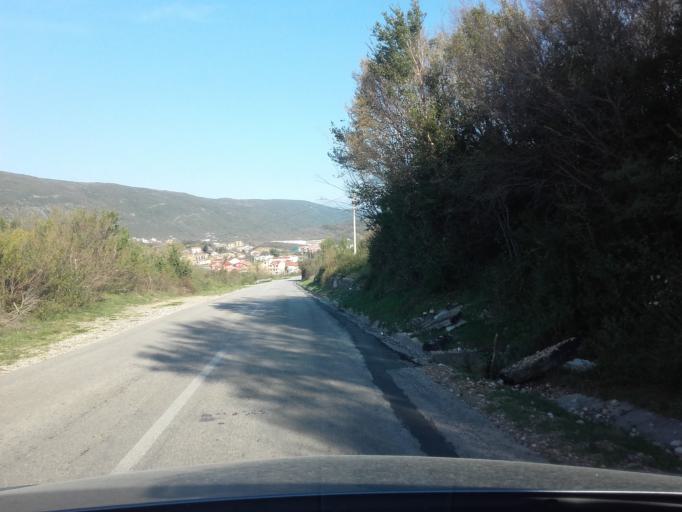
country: ME
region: Budva
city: Budva
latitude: 42.3037
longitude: 18.8090
